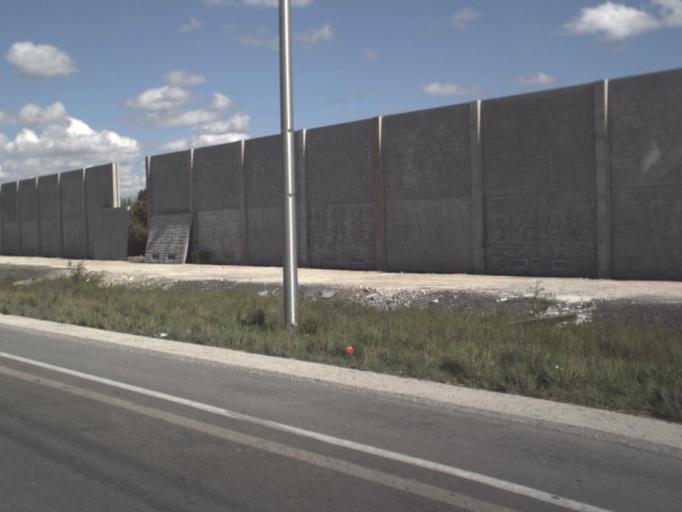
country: US
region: Florida
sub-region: Miami-Dade County
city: South Miami Heights
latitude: 25.6025
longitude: -80.3775
